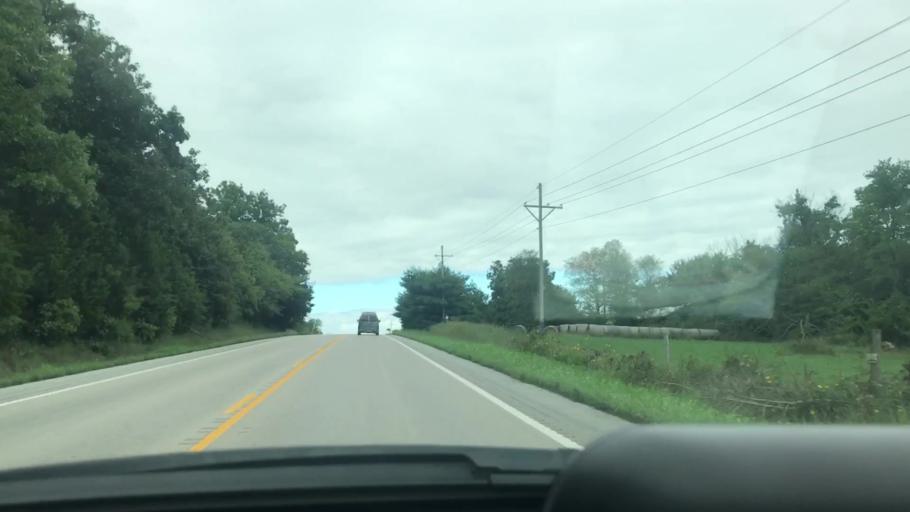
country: US
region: Missouri
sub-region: Hickory County
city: Hermitage
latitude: 37.8780
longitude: -93.1803
